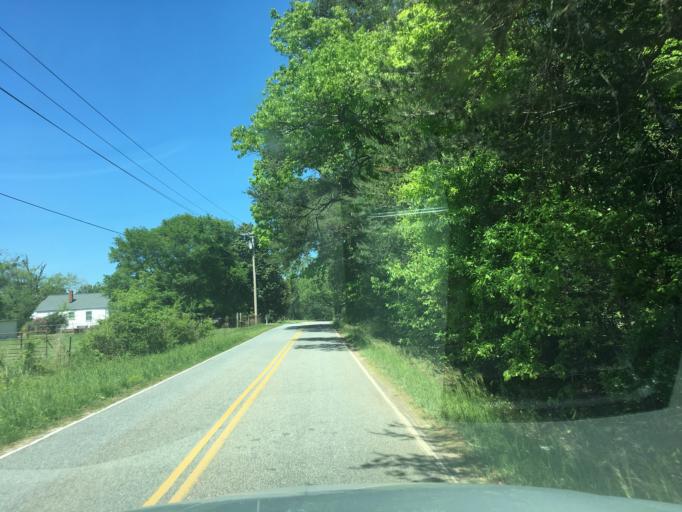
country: US
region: South Carolina
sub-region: Spartanburg County
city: Duncan
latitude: 34.8749
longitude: -82.1778
